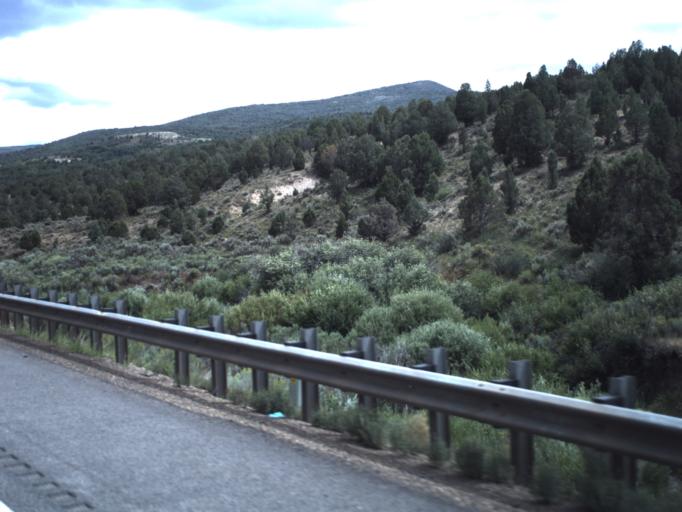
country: US
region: Utah
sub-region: Sanpete County
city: Fairview
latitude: 39.9295
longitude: -111.1944
